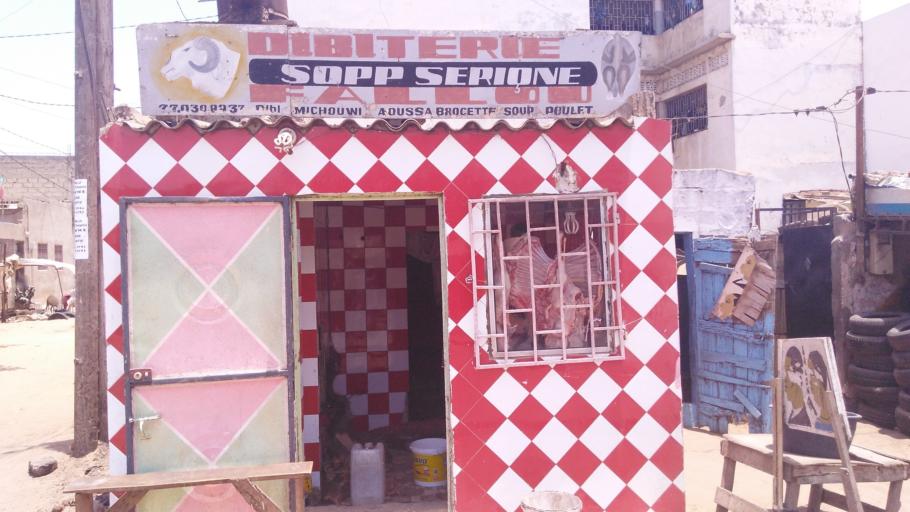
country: SN
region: Dakar
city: Pikine
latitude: 14.7817
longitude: -17.3757
